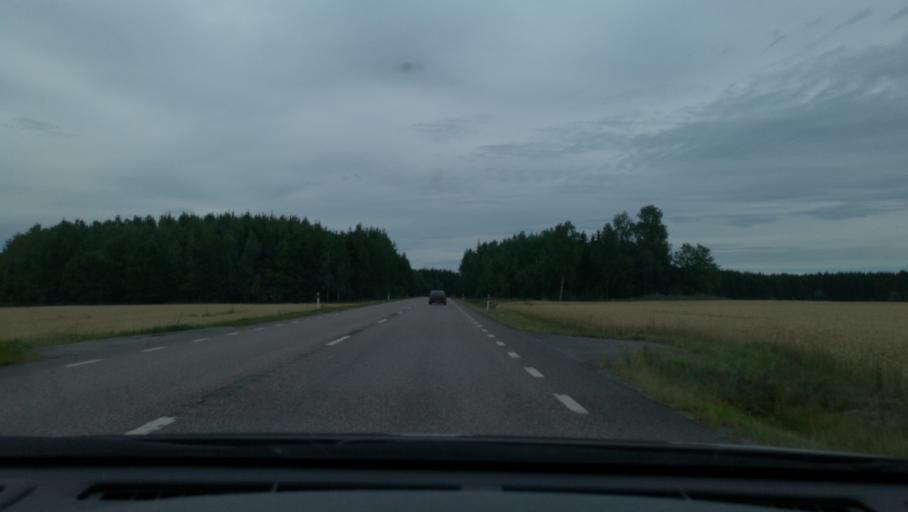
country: SE
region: Soedermanland
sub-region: Katrineholms Kommun
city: Katrineholm
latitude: 59.0230
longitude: 16.2141
